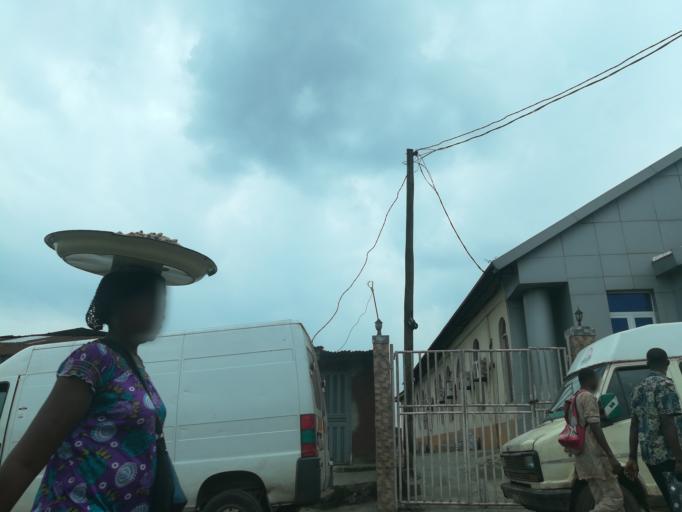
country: NG
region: Lagos
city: Ojota
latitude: 6.6112
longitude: 3.3961
